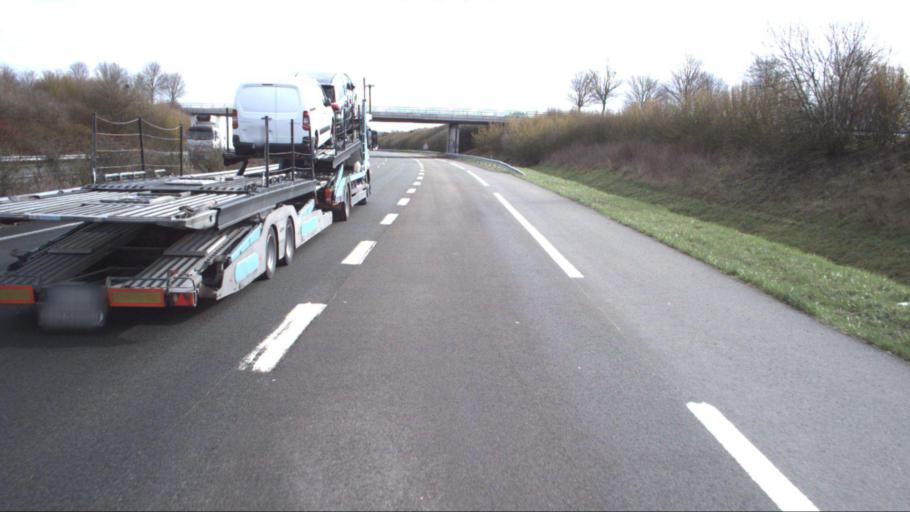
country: FR
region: Ile-de-France
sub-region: Departement des Yvelines
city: Houdan
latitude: 48.7829
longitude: 1.6157
